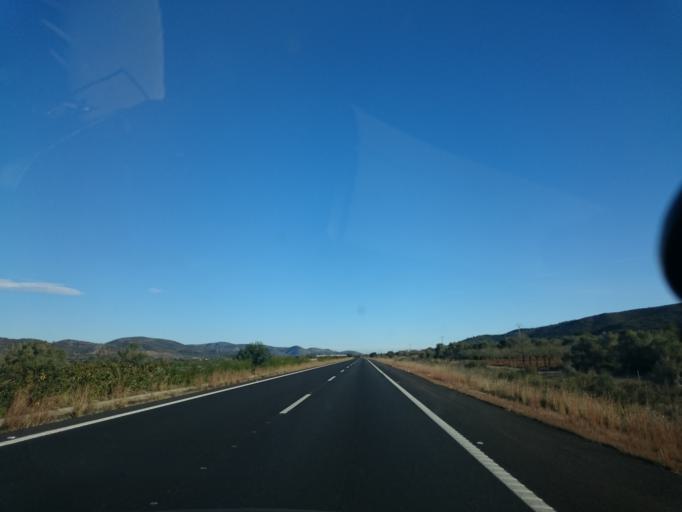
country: ES
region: Valencia
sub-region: Provincia de Castello
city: Alcala de Xivert
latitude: 40.3140
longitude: 0.2456
